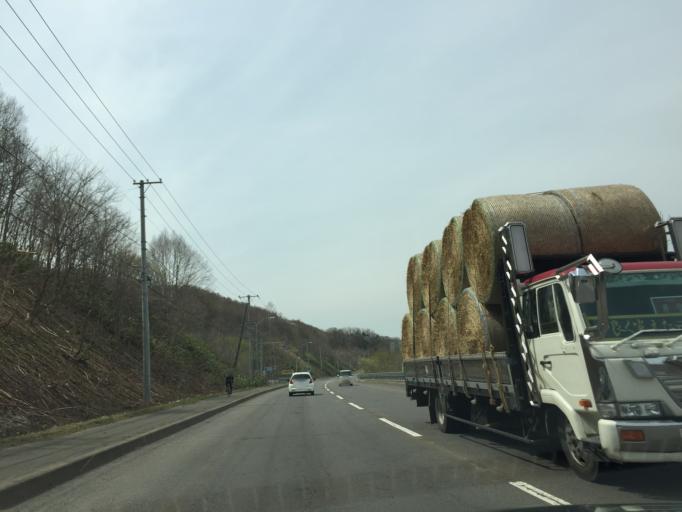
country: JP
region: Hokkaido
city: Ashibetsu
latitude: 43.5338
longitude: 142.1509
